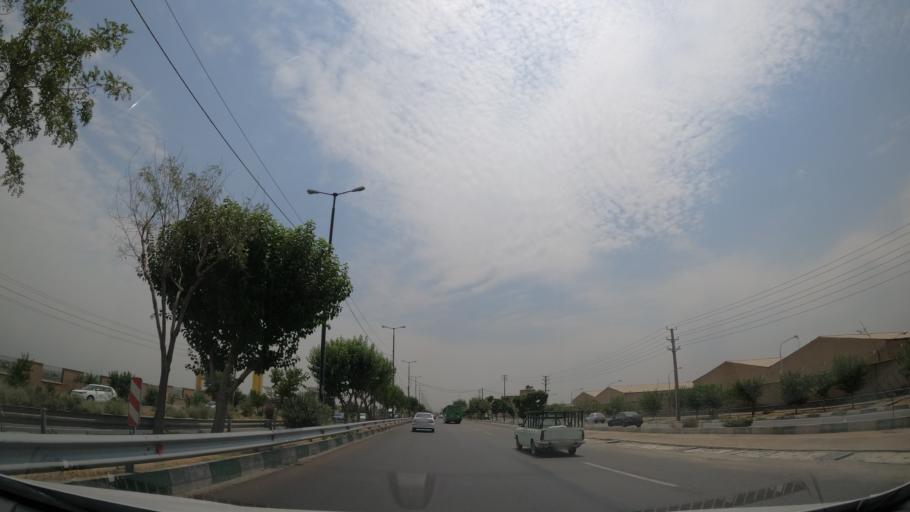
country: IR
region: Tehran
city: Eslamshahr
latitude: 35.6814
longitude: 51.2416
